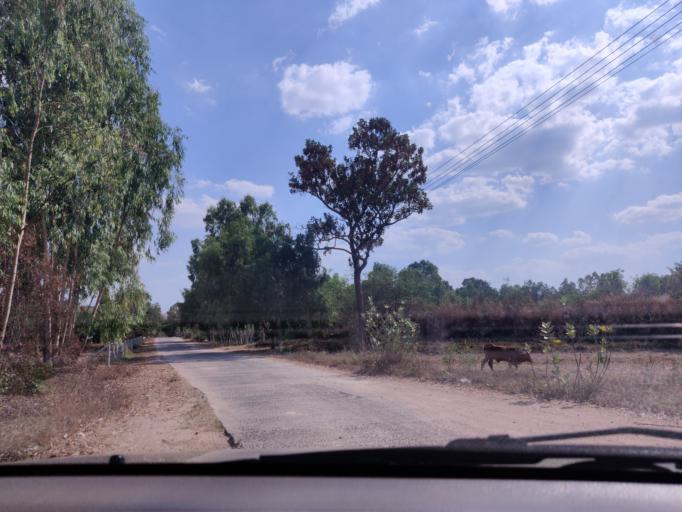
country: TH
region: Sisaket
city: Si Sa Ket
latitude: 15.0706
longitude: 104.3492
